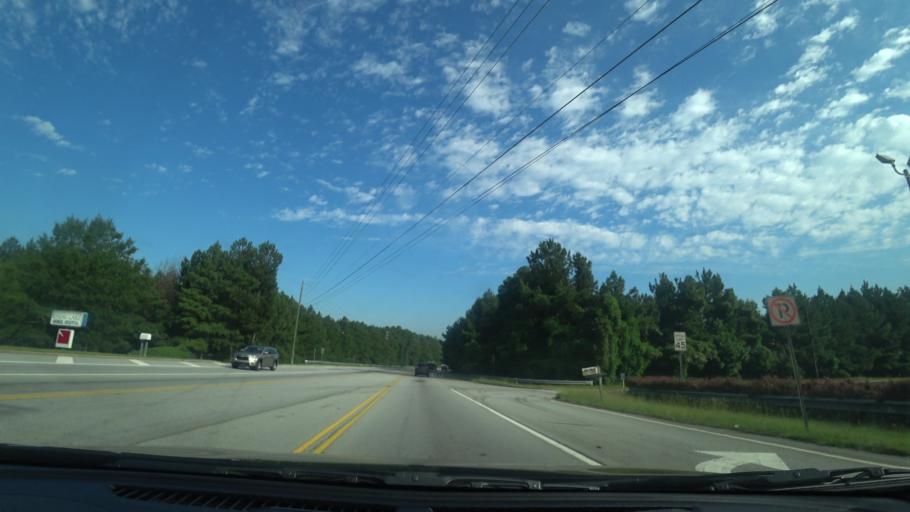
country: US
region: Georgia
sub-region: Rockdale County
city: Conyers
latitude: 33.6709
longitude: -83.9878
